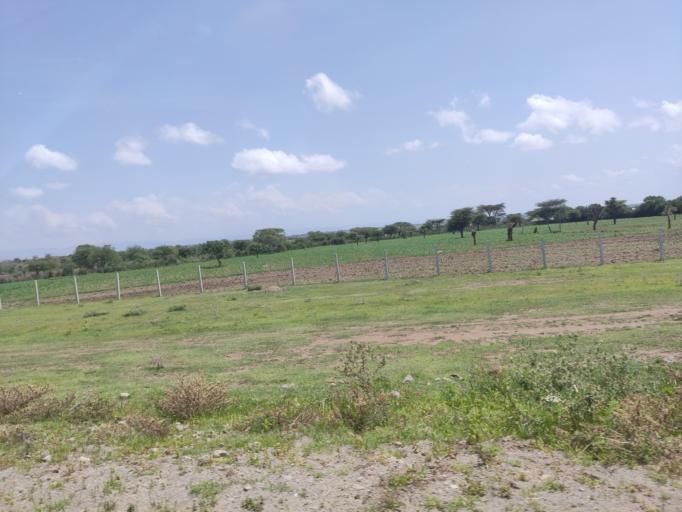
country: ET
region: Oromiya
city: Ziway
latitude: 8.2582
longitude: 38.8970
